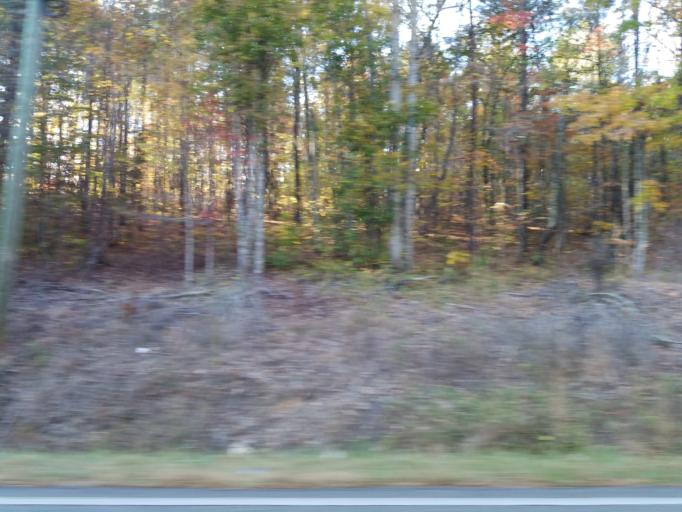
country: US
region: Georgia
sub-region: Pickens County
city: Jasper
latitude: 34.5662
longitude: -84.4733
